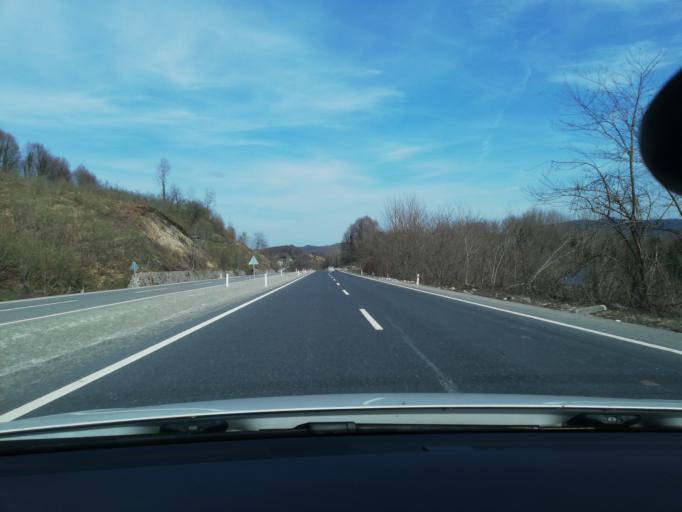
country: TR
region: Zonguldak
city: Ormanli
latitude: 41.3303
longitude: 31.6020
